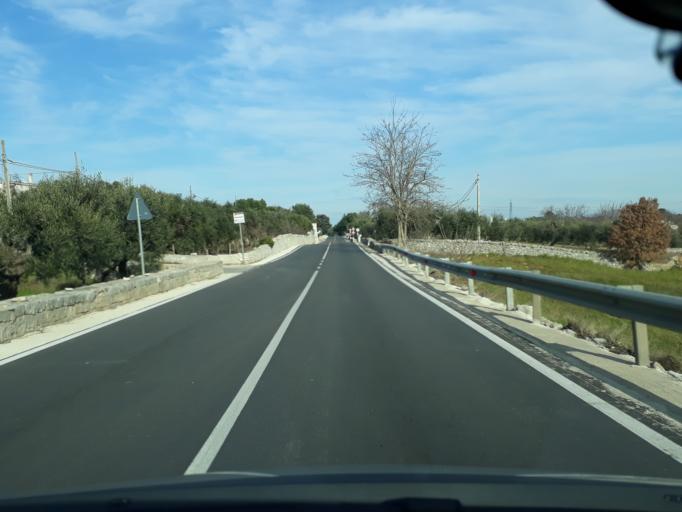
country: IT
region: Apulia
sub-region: Provincia di Brindisi
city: Lamie di Olimpie-Selva
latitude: 40.7860
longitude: 17.3415
